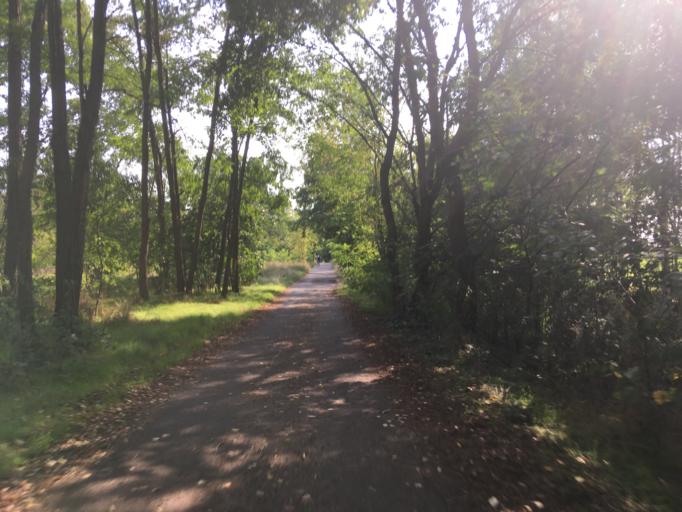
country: DE
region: Berlin
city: Frohnau
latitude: 52.6469
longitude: 13.2834
